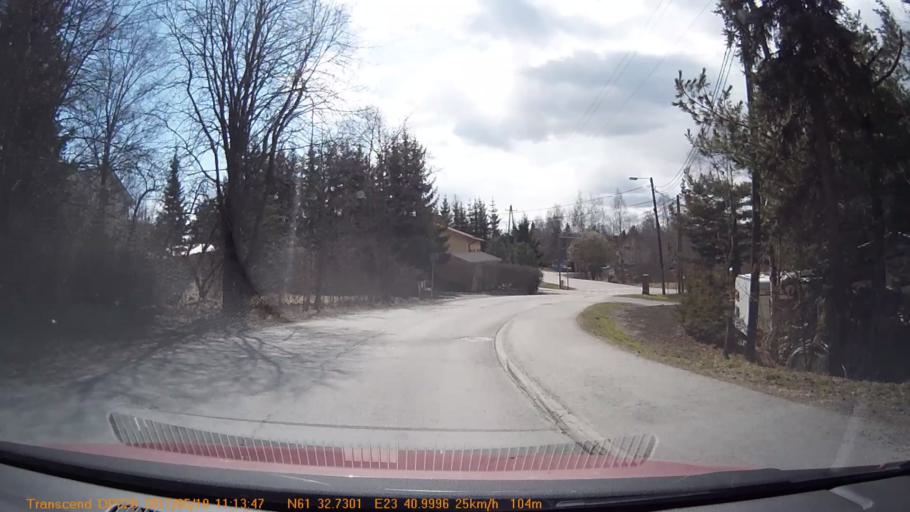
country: FI
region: Pirkanmaa
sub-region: Tampere
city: Yloejaervi
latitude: 61.5456
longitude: 23.6833
